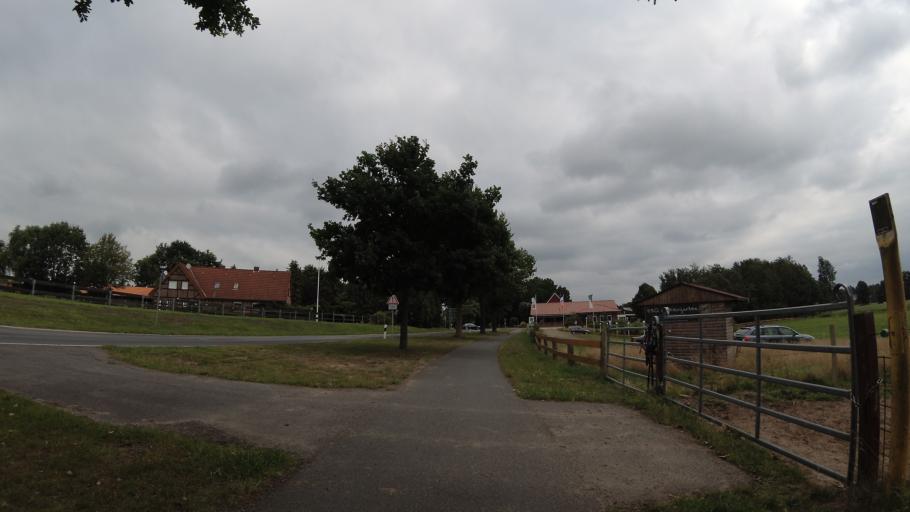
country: DE
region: Lower Saxony
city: Oberlangen
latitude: 52.8469
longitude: 7.2664
